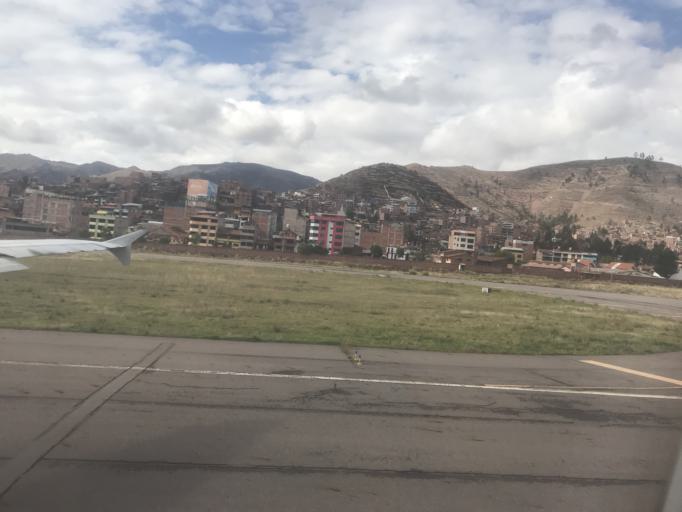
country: PE
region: Cusco
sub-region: Provincia de Cusco
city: Cusco
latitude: -13.5342
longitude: -71.9537
